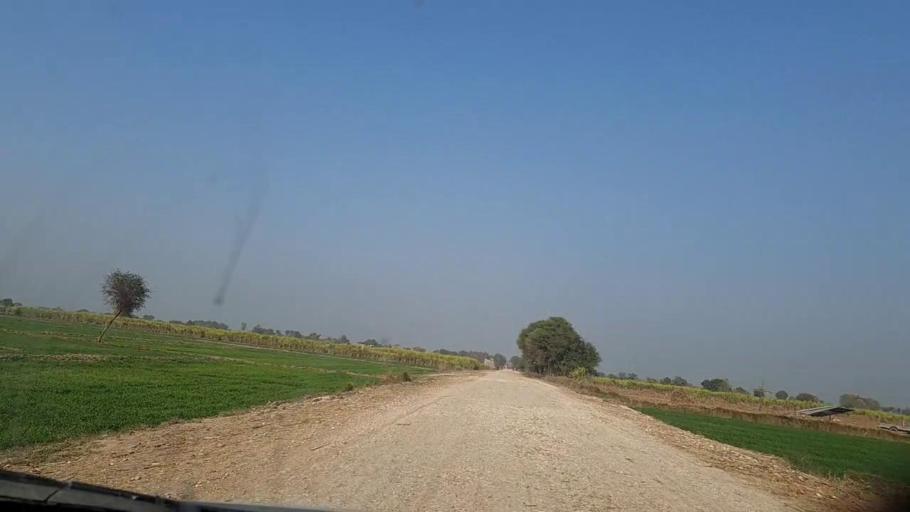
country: PK
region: Sindh
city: Moro
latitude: 26.7808
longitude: 67.9360
